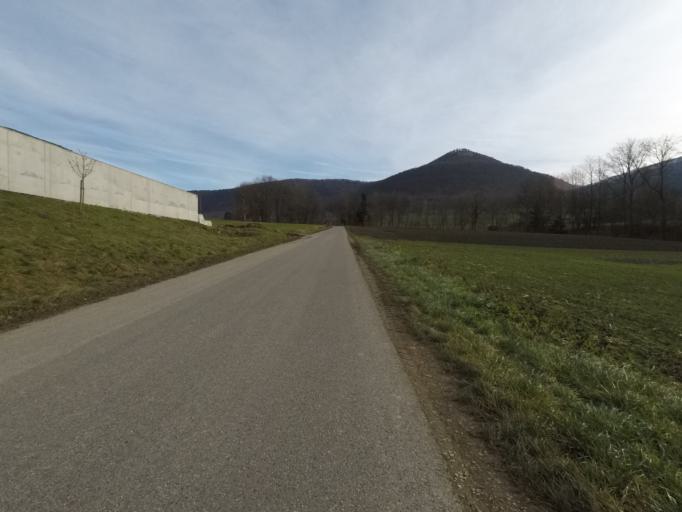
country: DE
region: Baden-Wuerttemberg
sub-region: Tuebingen Region
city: Eningen unter Achalm
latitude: 48.4709
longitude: 9.2676
